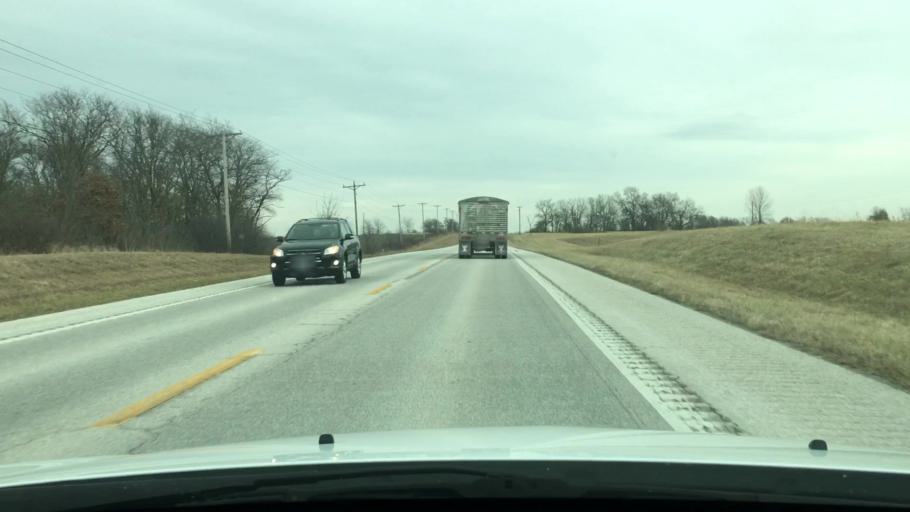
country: US
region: Missouri
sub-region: Pike County
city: Bowling Green
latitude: 39.3443
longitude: -91.2744
